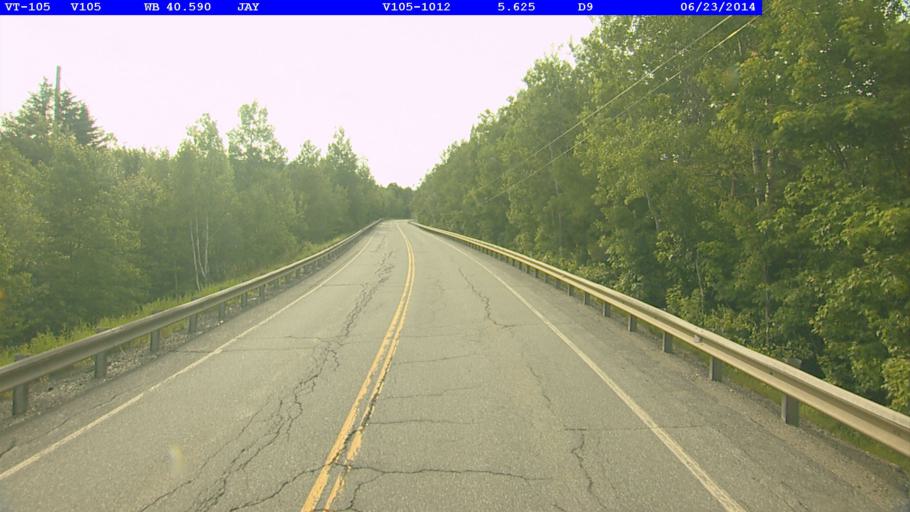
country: CA
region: Quebec
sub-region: Monteregie
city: Sutton
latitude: 44.9766
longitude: -72.4734
